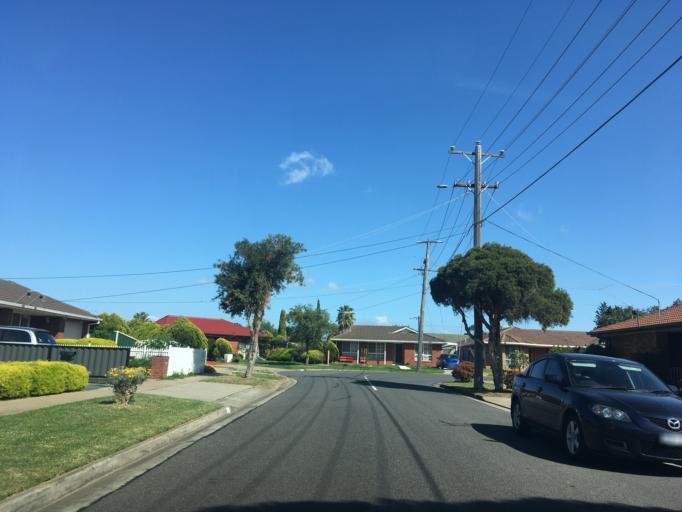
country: AU
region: Victoria
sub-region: Wyndham
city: Hoppers Crossing
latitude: -37.8756
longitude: 144.7042
